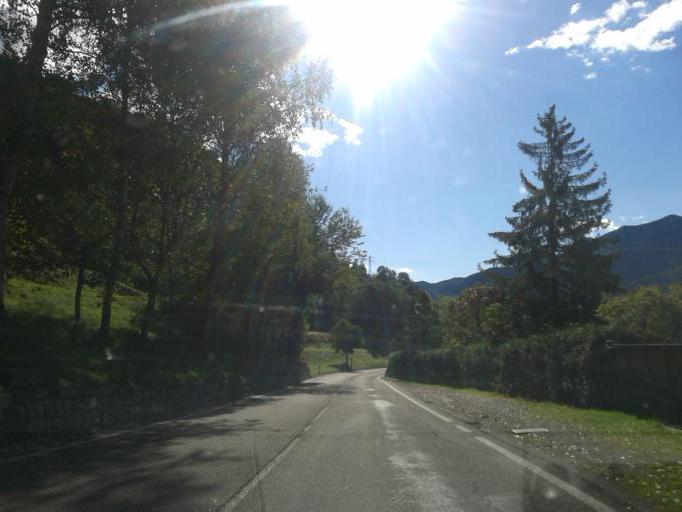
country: IT
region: Trentino-Alto Adige
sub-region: Provincia di Trento
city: Pieve di Ledro
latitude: 45.8851
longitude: 10.7456
